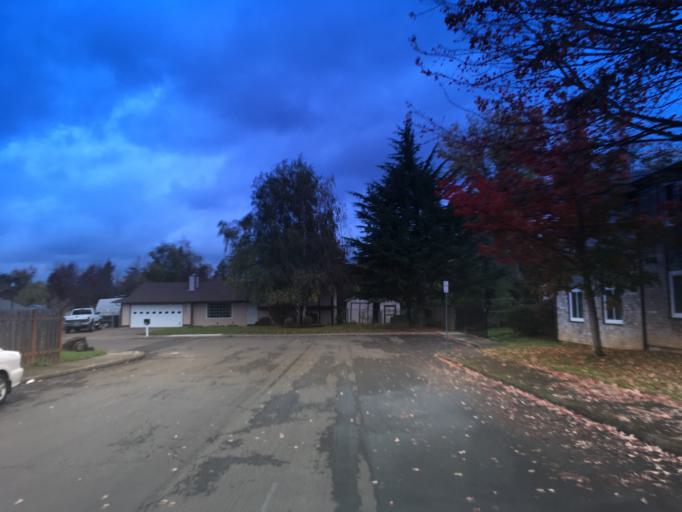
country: US
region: Oregon
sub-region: Multnomah County
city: Fairview
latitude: 45.5371
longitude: -122.4296
